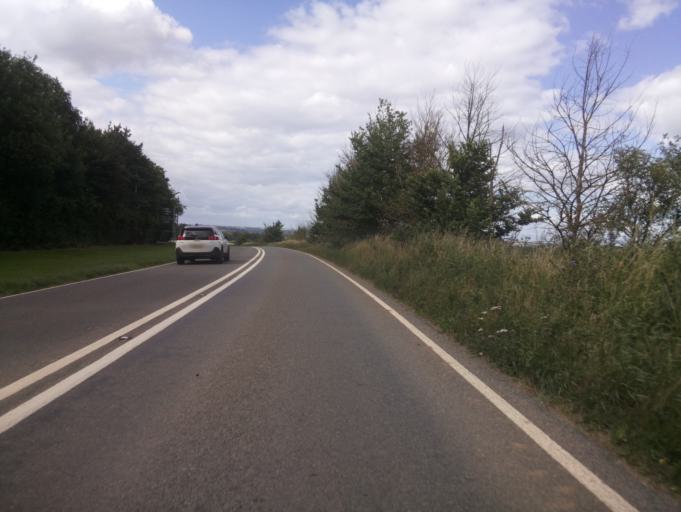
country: GB
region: England
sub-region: Leicestershire
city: Measham
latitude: 52.6664
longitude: -1.5385
